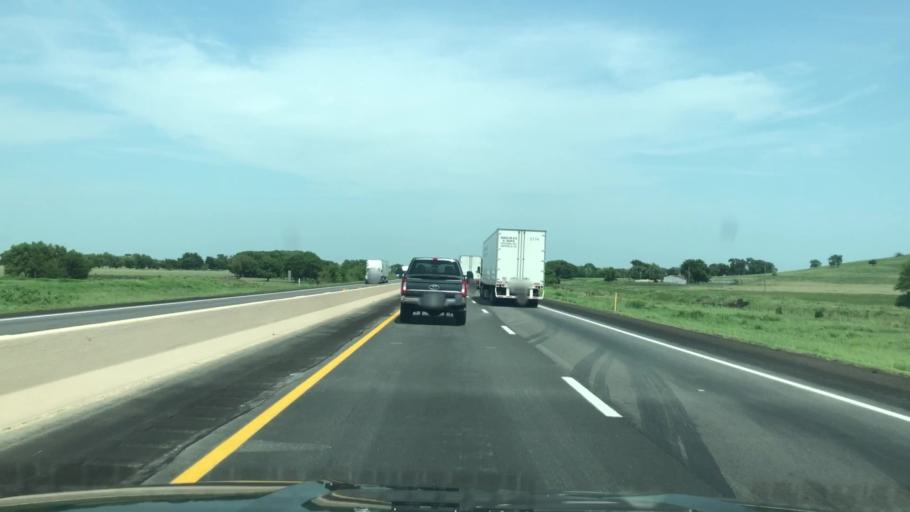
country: US
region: Oklahoma
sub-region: Ottawa County
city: Afton
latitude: 36.6839
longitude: -95.0346
